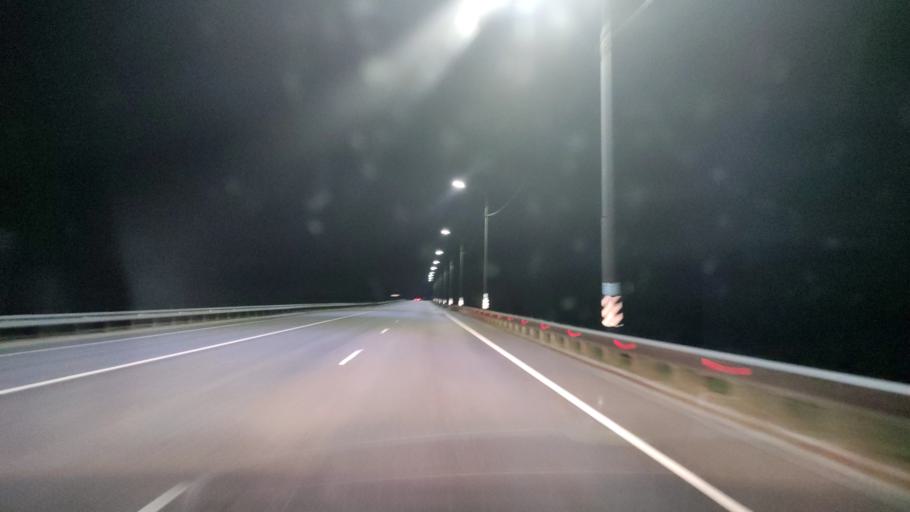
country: RU
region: Voronezj
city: Nizhnedevitsk
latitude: 51.5723
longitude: 38.4777
